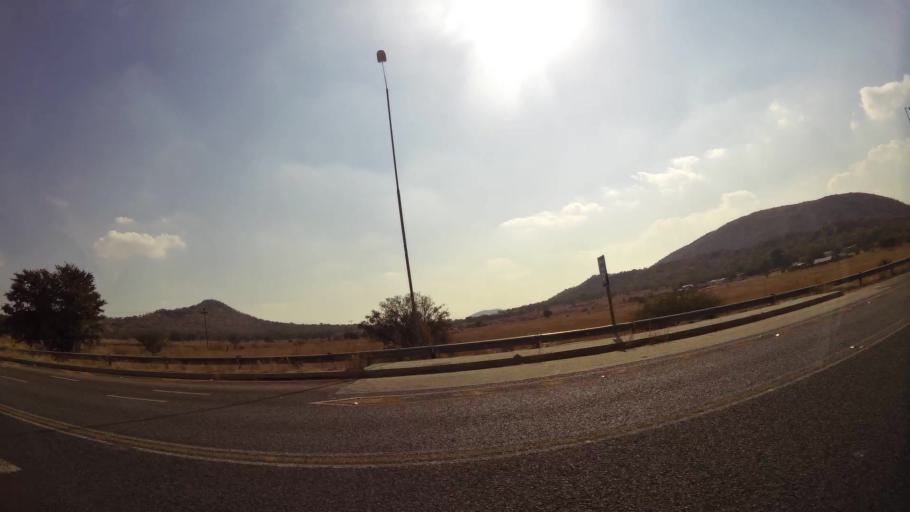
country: ZA
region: North-West
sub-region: Bojanala Platinum District Municipality
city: Rustenburg
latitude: -25.5826
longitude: 27.1335
